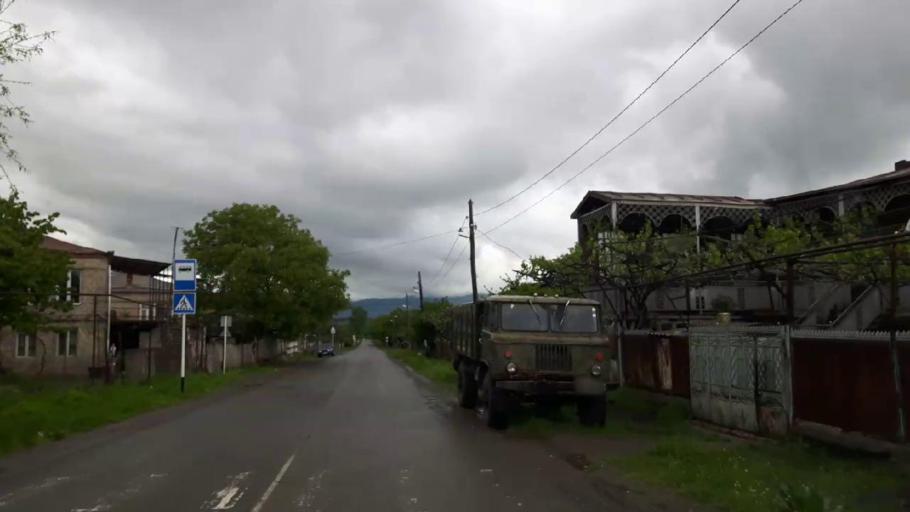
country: GE
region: Shida Kartli
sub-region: Khashuris Raioni
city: Khashuri
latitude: 41.9848
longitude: 43.6632
